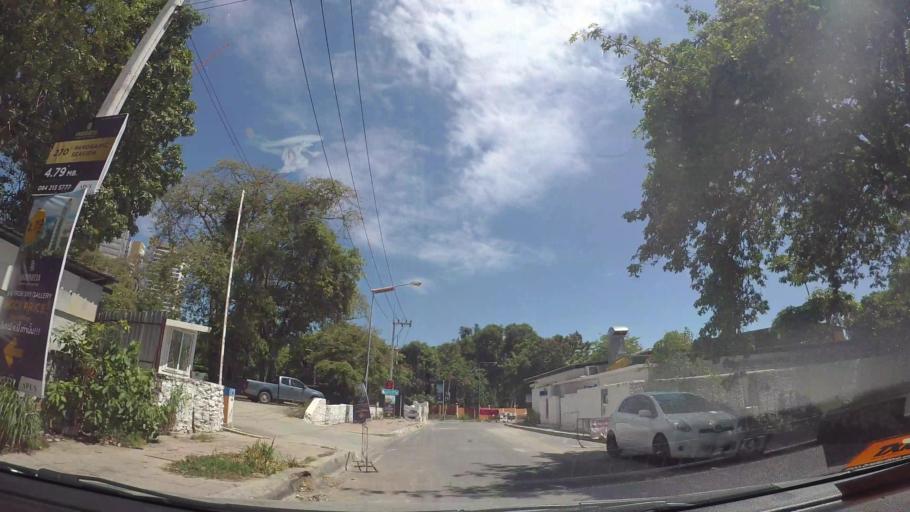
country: TH
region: Chon Buri
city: Phatthaya
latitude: 12.9204
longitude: 100.8593
